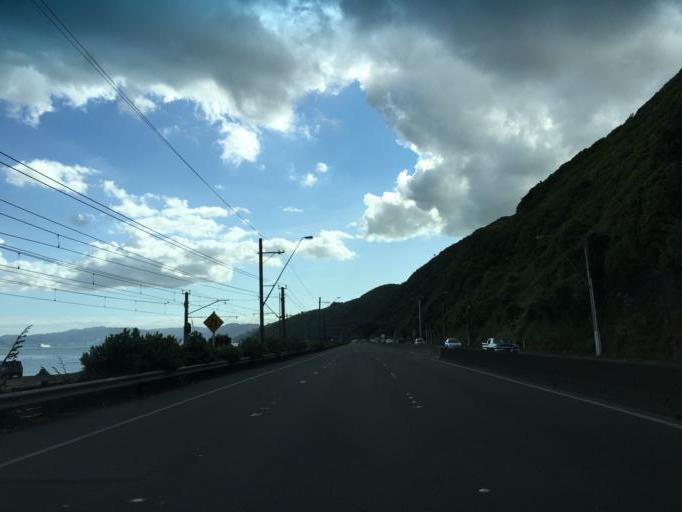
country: NZ
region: Wellington
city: Petone
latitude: -41.2247
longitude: 174.8565
